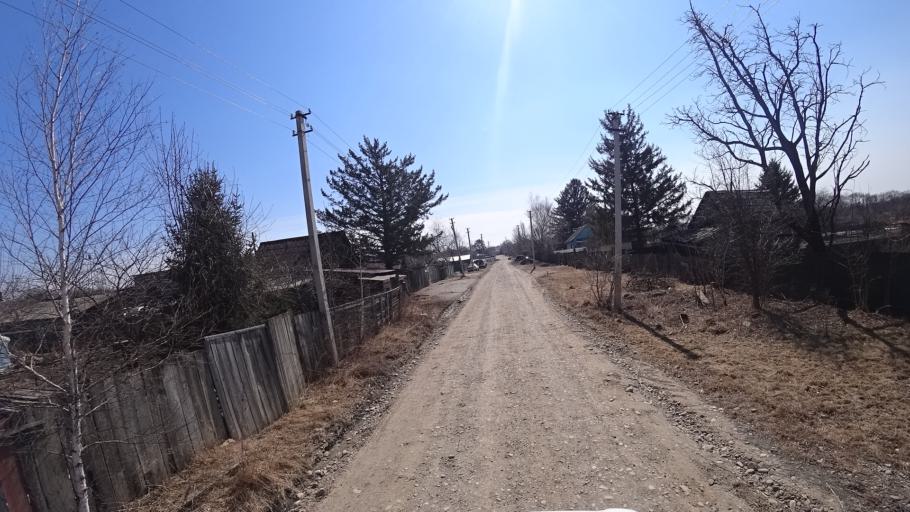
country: RU
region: Amur
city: Novobureyskiy
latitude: 49.7896
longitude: 129.8535
